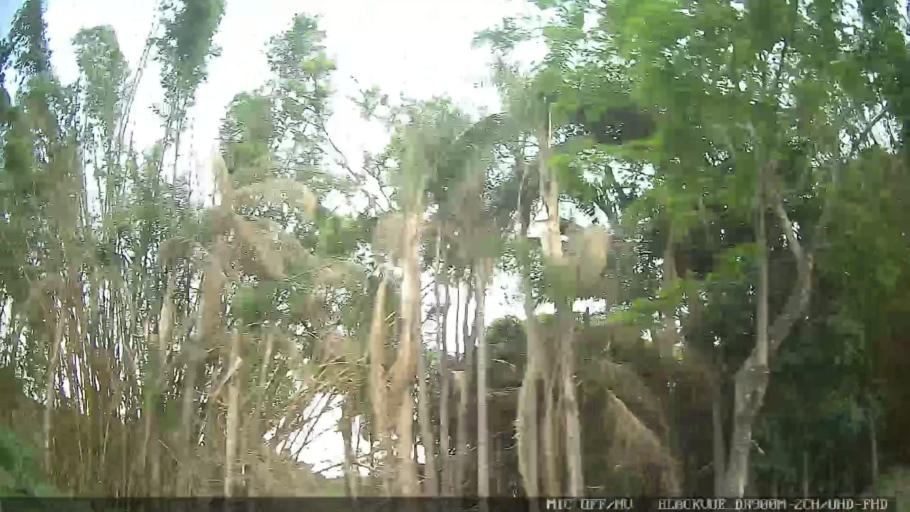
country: BR
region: Sao Paulo
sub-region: Amparo
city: Amparo
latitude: -22.8505
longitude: -46.7825
